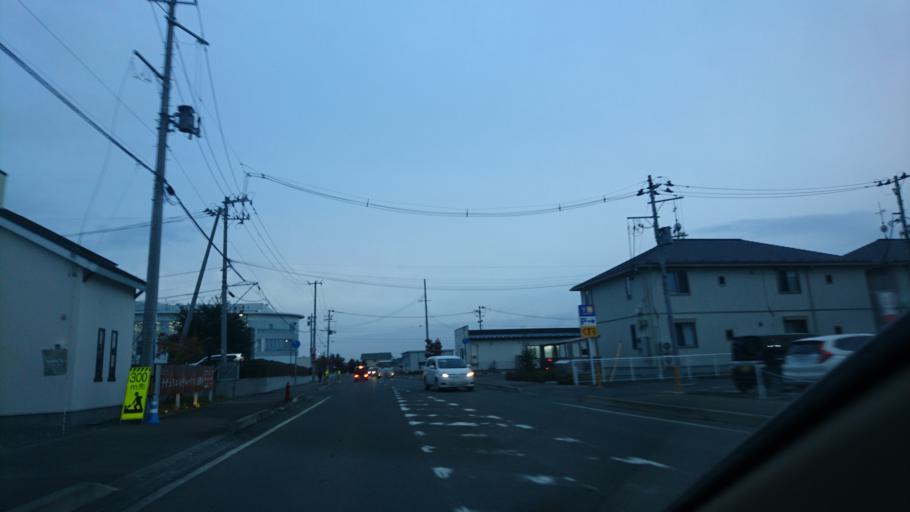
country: JP
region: Iwate
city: Morioka-shi
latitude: 39.6723
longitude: 141.1319
